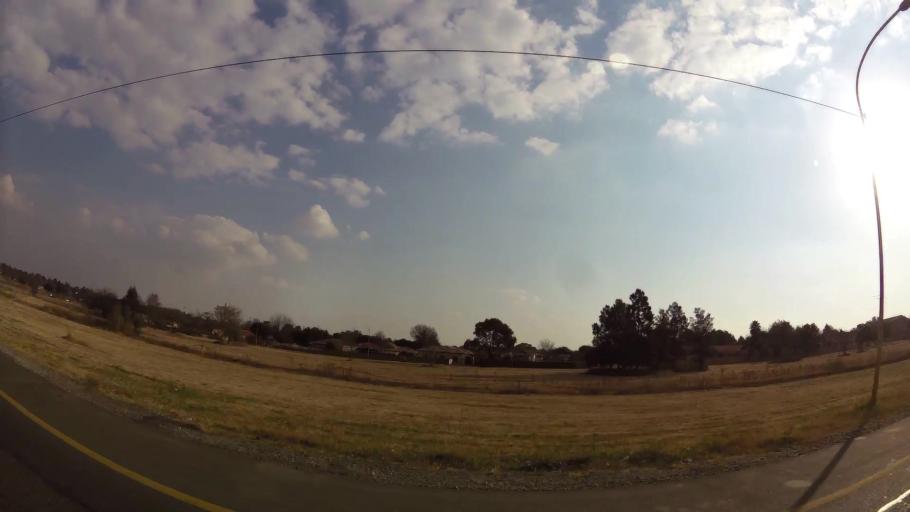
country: ZA
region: Gauteng
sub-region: Ekurhuleni Metropolitan Municipality
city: Springs
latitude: -26.2769
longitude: 28.4523
